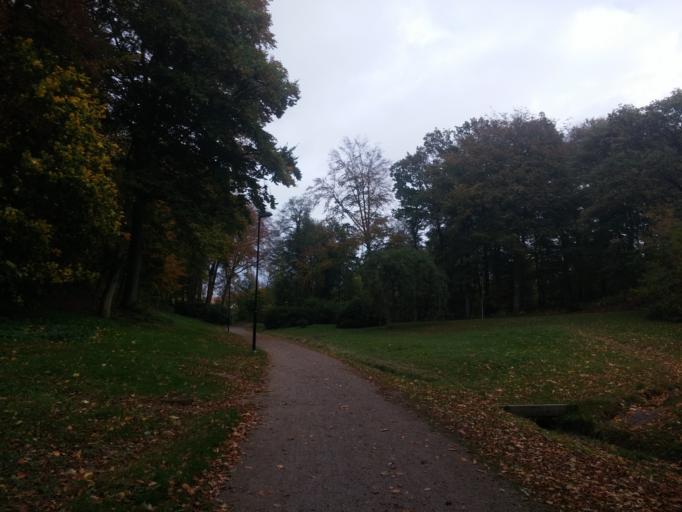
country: SE
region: Halland
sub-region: Laholms Kommun
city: Laholm
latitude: 56.5061
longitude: 13.0415
